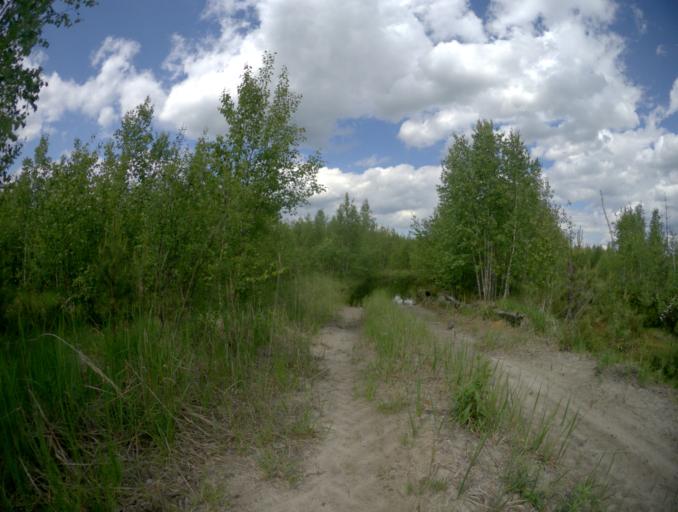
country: RU
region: Vladimir
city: Velikodvorskiy
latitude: 55.2749
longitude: 40.8736
